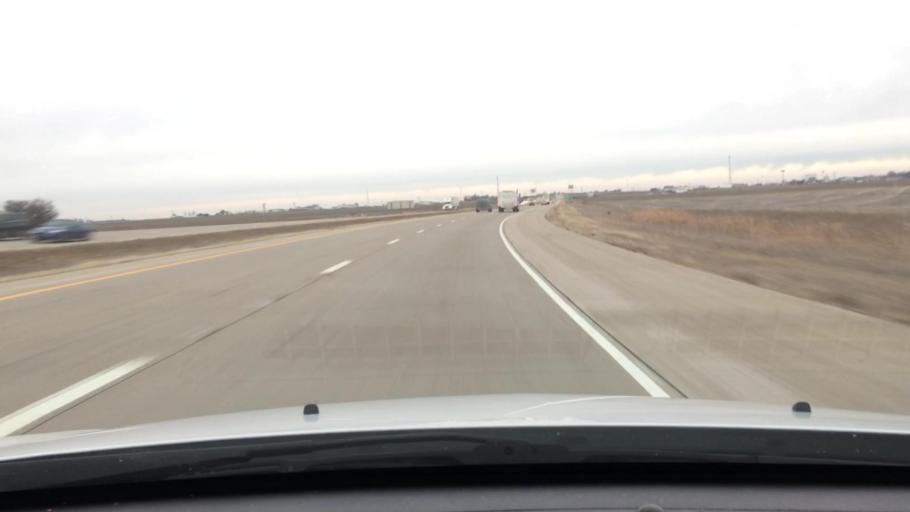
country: US
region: Illinois
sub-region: Woodford County
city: El Paso
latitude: 40.7169
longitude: -89.0339
